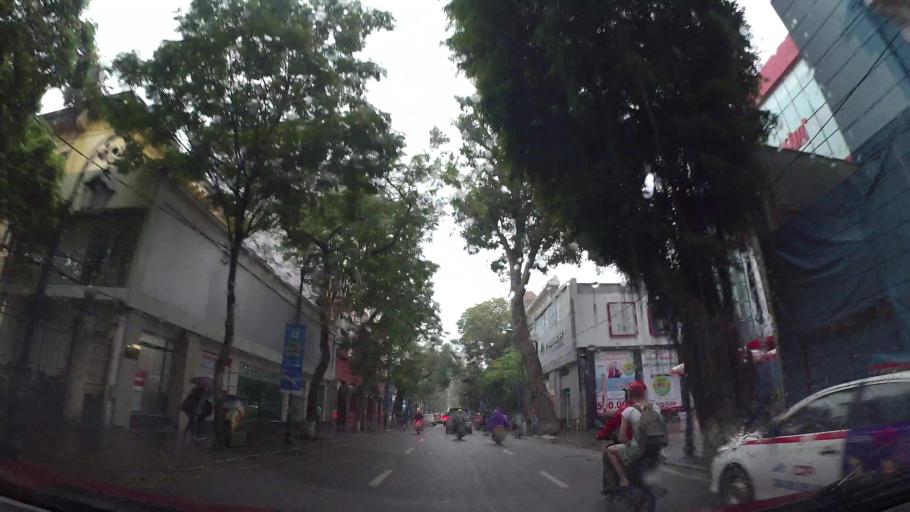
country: VN
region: Ha Noi
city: Hoan Kiem
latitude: 21.0266
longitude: 105.8492
